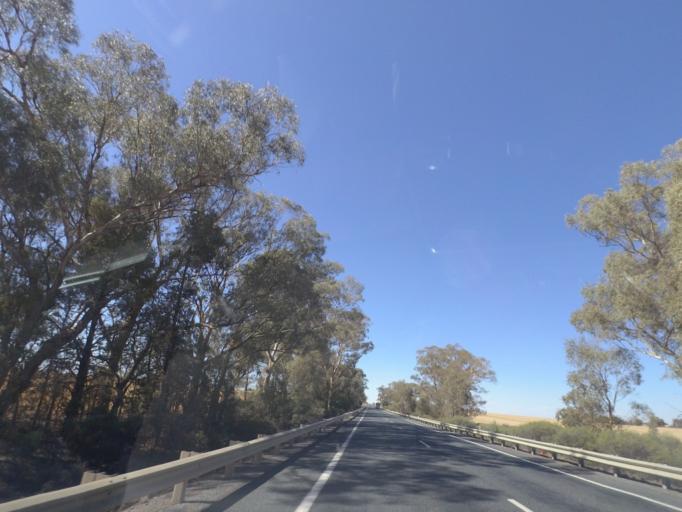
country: AU
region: New South Wales
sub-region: Bland
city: West Wyalong
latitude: -34.1749
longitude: 147.1144
